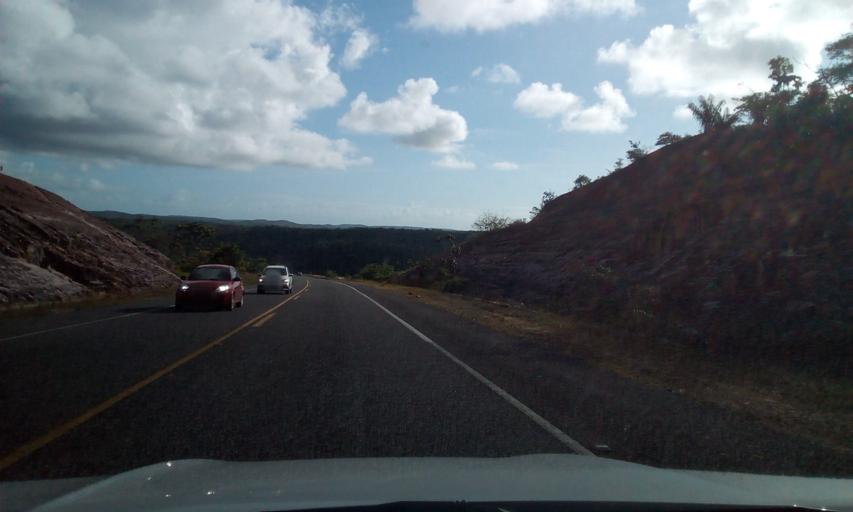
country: BR
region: Bahia
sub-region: Conde
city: Conde
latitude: -12.0789
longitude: -37.7592
